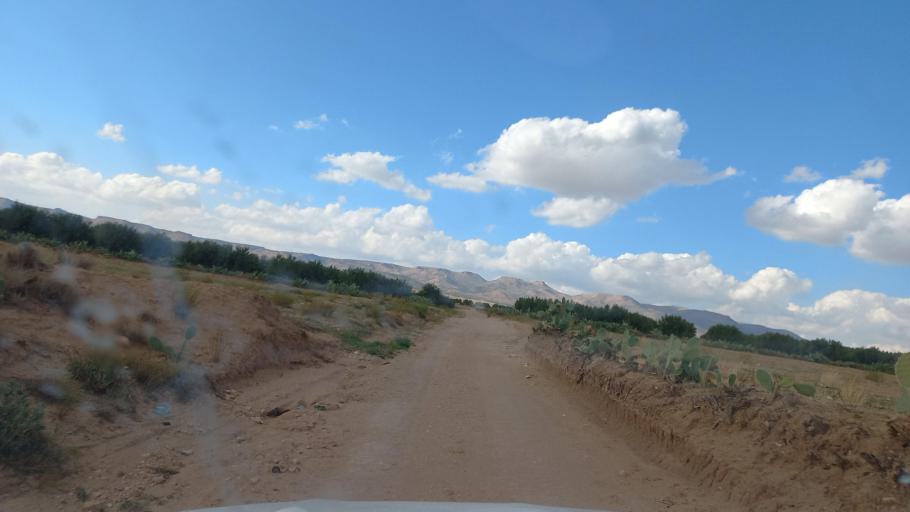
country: TN
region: Al Qasrayn
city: Sbiba
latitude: 35.3902
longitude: 9.0390
